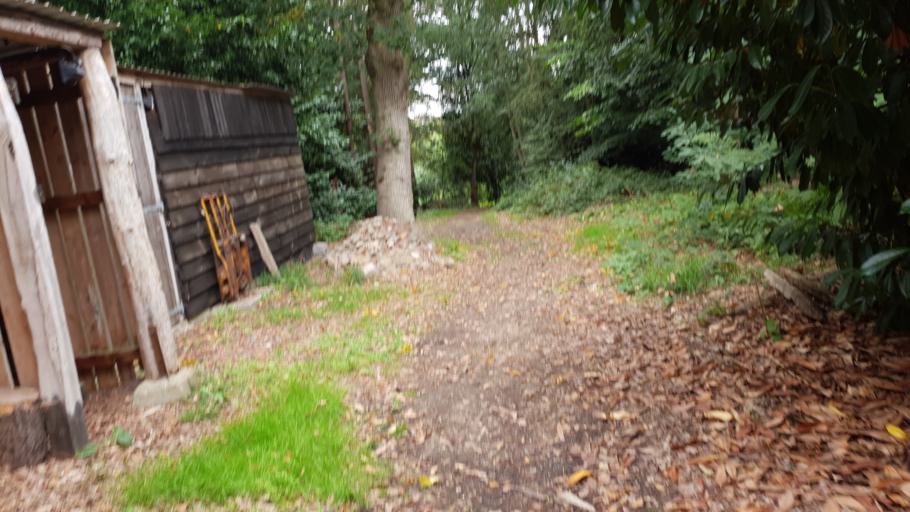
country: GB
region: England
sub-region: Suffolk
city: East Bergholt
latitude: 51.9409
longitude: 1.0170
